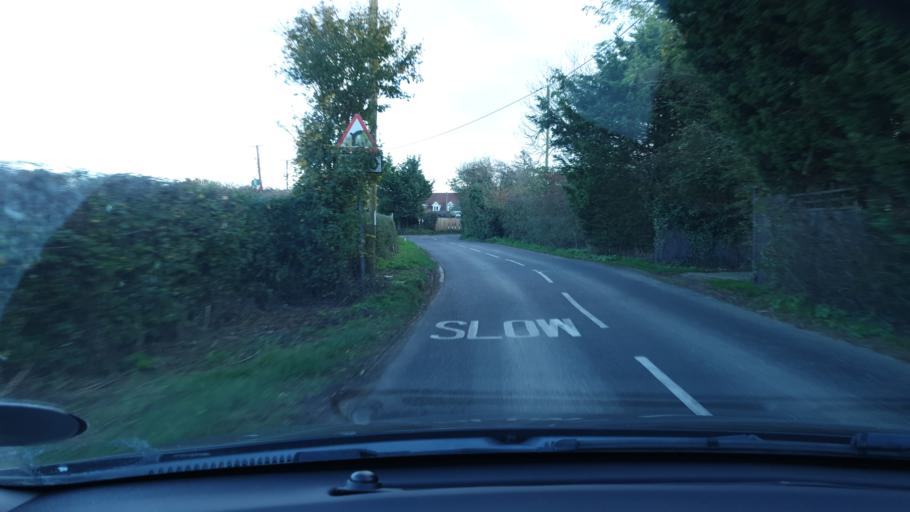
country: GB
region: England
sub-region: Essex
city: Little Clacton
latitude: 51.8970
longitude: 1.1462
